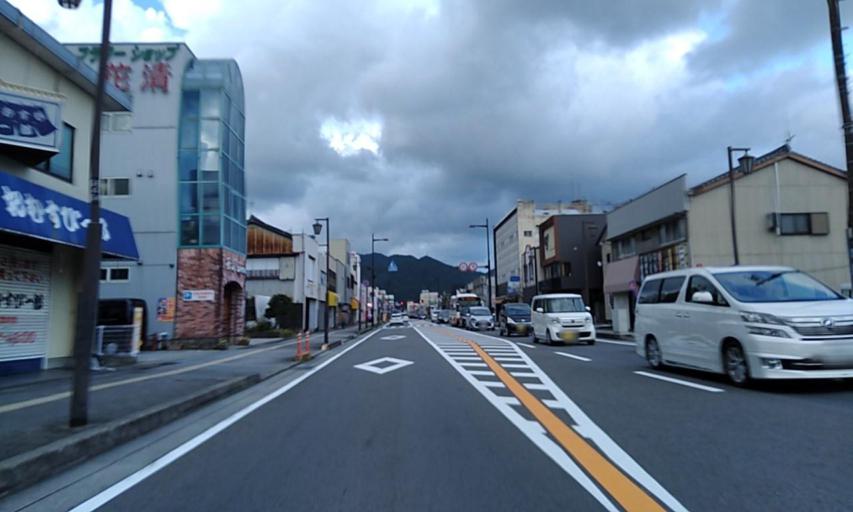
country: JP
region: Wakayama
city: Shingu
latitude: 33.7225
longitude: 135.9865
